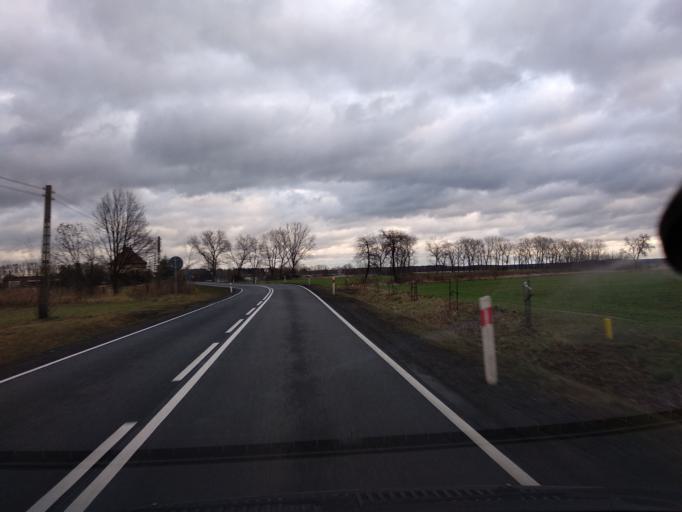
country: PL
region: Lower Silesian Voivodeship
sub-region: Powiat olesnicki
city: Miedzyborz
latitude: 51.4130
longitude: 17.6729
